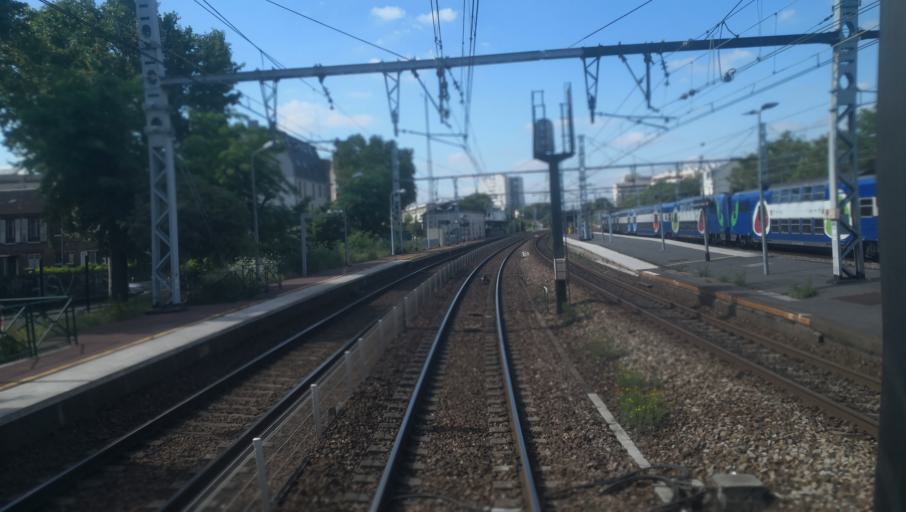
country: FR
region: Ile-de-France
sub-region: Departement du Val-de-Marne
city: Alfortville
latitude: 48.8008
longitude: 2.4269
